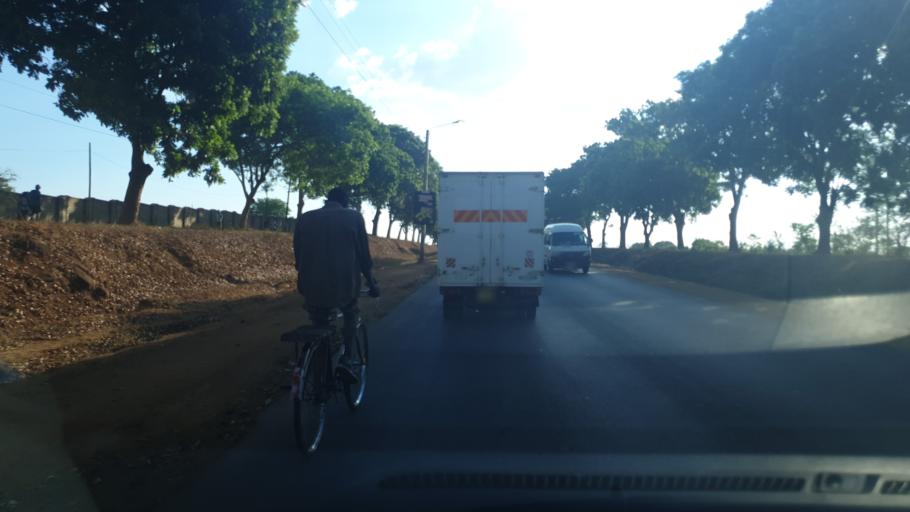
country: MW
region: Central Region
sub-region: Lilongwe District
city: Lilongwe
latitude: -13.9726
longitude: 33.7822
